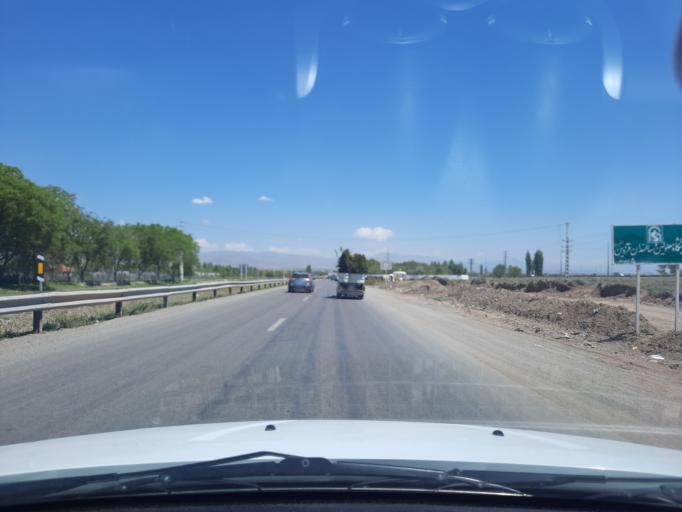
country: IR
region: Qazvin
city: Qazvin
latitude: 36.2624
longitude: 50.0516
